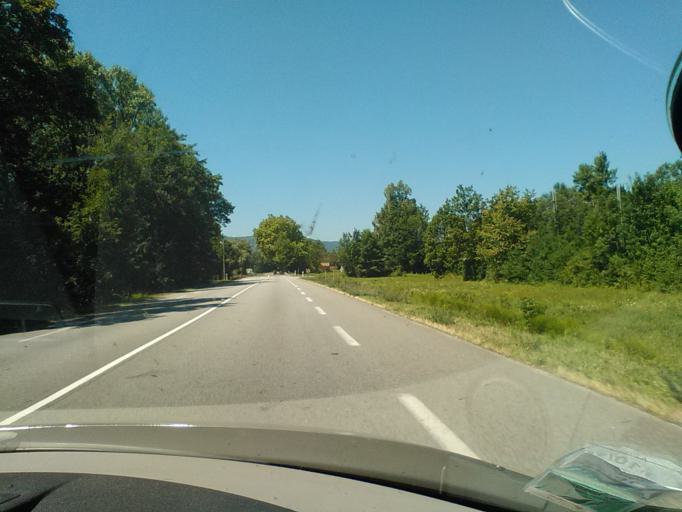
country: FR
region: Rhone-Alpes
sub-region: Departement de la Savoie
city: Les Marches
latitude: 45.5070
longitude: 6.0253
